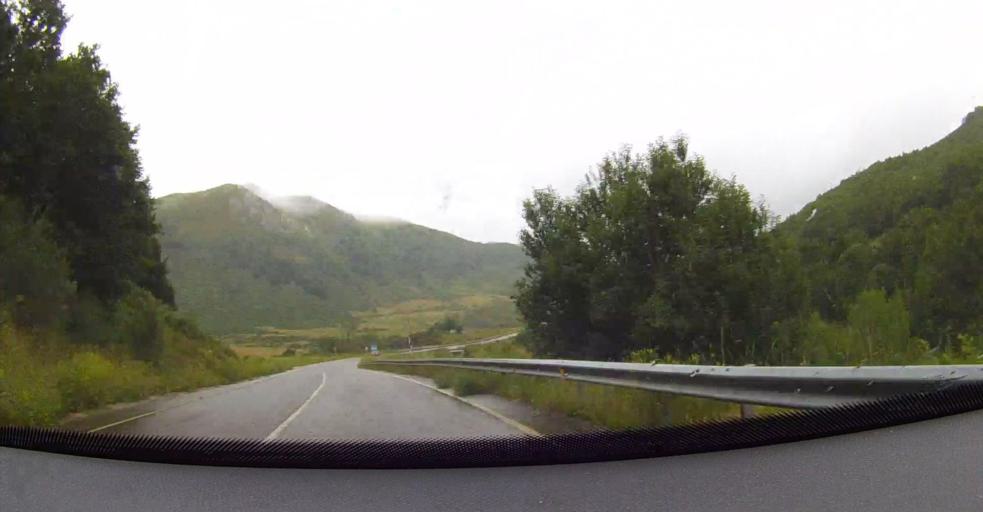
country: ES
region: Castille and Leon
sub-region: Provincia de Leon
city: Marana
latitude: 43.0722
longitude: -5.1594
